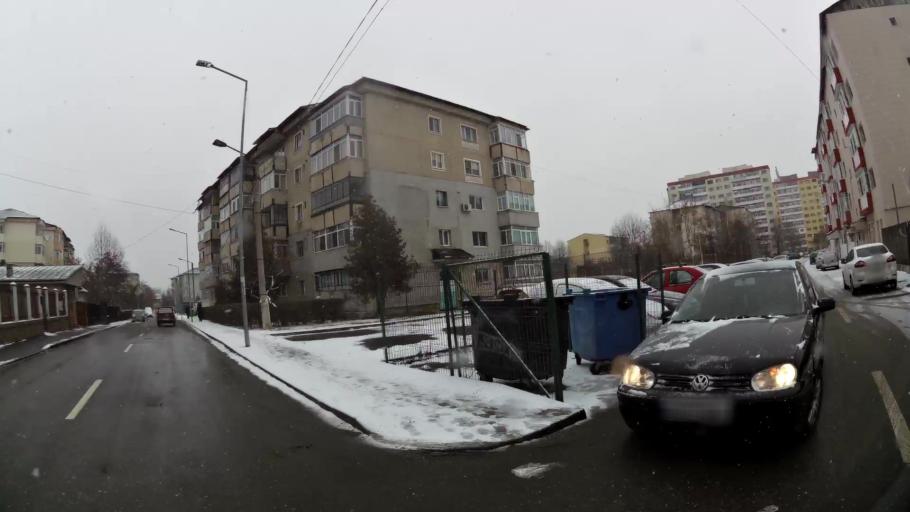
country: RO
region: Dambovita
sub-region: Municipiul Targoviste
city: Targoviste
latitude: 44.9253
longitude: 25.4409
